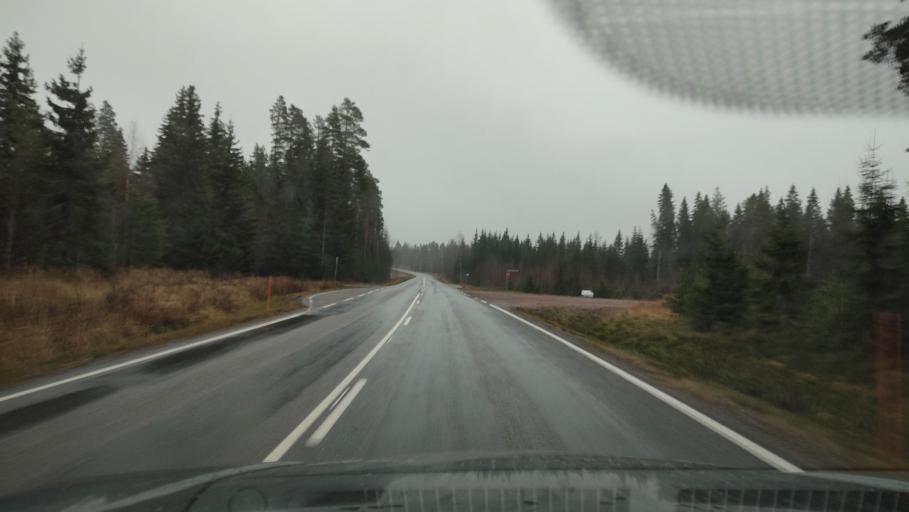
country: FI
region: Southern Ostrobothnia
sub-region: Suupohja
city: Karijoki
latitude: 62.2219
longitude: 21.7434
